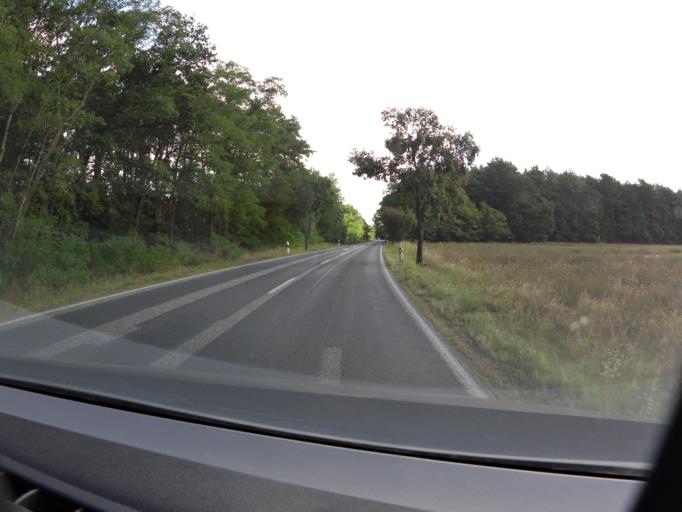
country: DE
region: Brandenburg
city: Storkow
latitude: 52.2706
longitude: 13.9474
